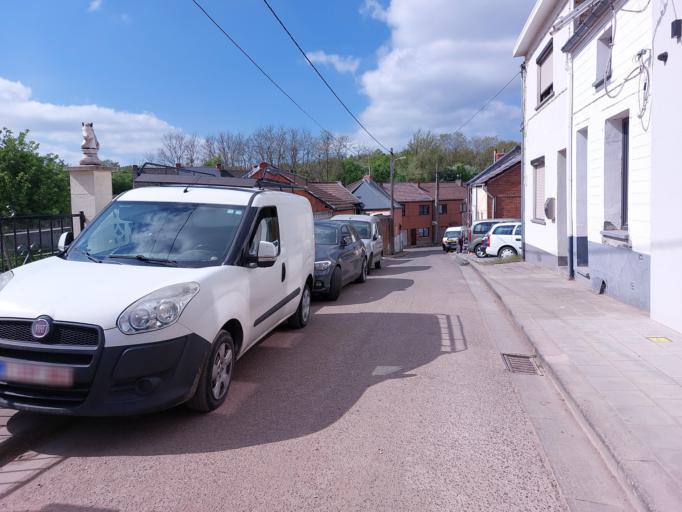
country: BE
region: Wallonia
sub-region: Province du Hainaut
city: Quaregnon
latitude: 50.4327
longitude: 3.8766
